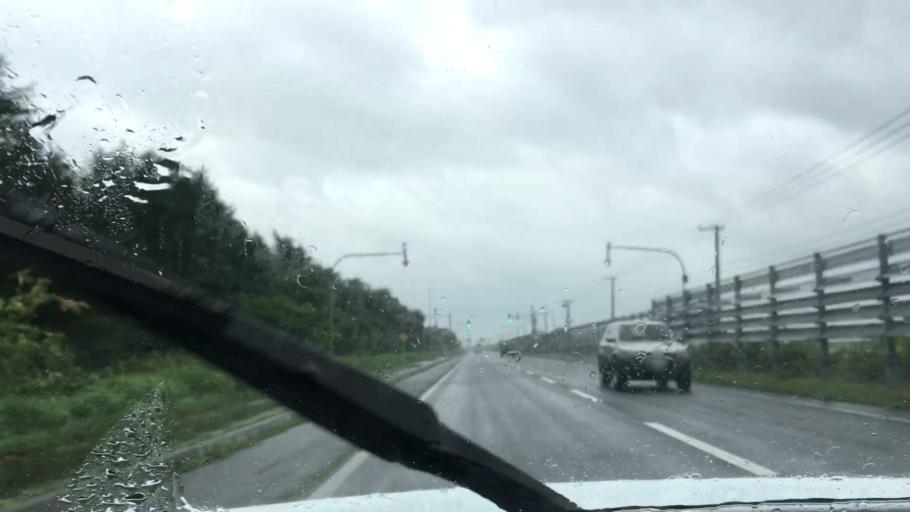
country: JP
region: Hokkaido
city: Nanae
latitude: 42.3093
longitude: 140.2729
